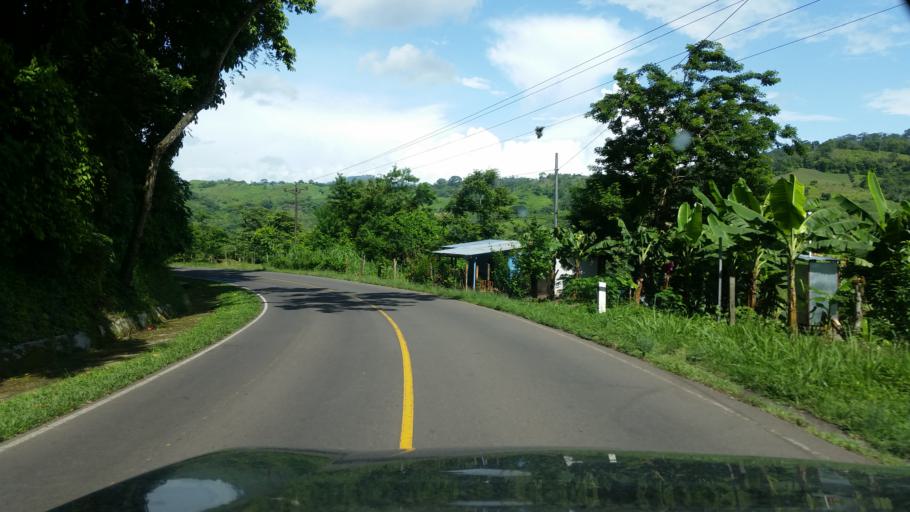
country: NI
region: Matagalpa
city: San Ramon
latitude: 13.0052
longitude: -85.8038
